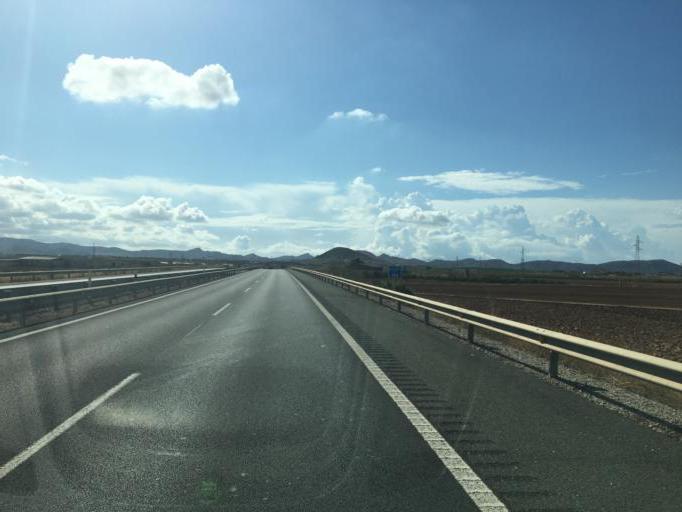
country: ES
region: Murcia
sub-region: Murcia
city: Cartagena
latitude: 37.6504
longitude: -0.9749
